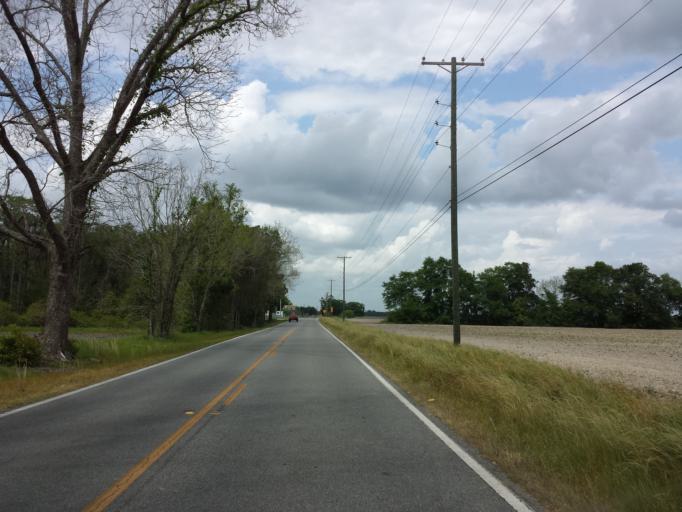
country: US
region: Georgia
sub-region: Lowndes County
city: Hahira
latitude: 31.0538
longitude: -83.3937
